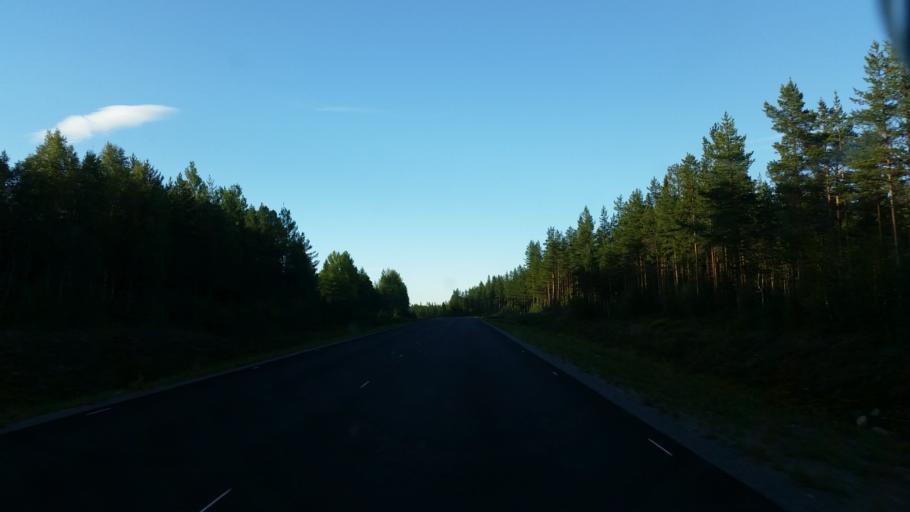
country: SE
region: Vaesterbotten
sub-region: Dorotea Kommun
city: Dorotea
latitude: 64.2698
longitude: 16.4991
